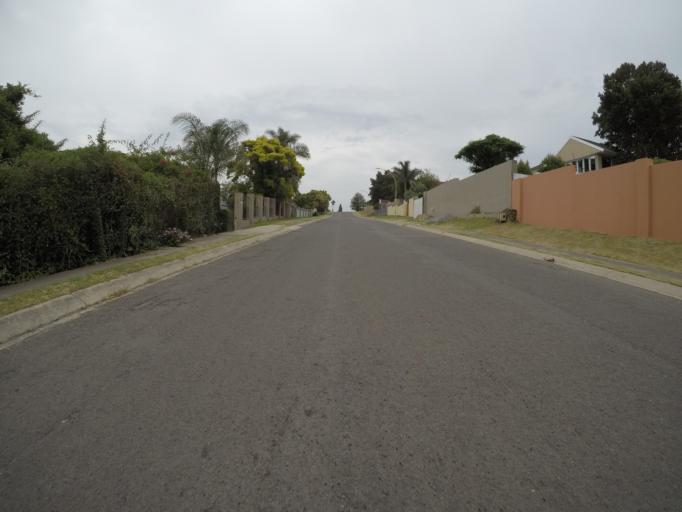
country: ZA
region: Eastern Cape
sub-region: Buffalo City Metropolitan Municipality
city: East London
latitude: -32.9962
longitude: 27.8597
